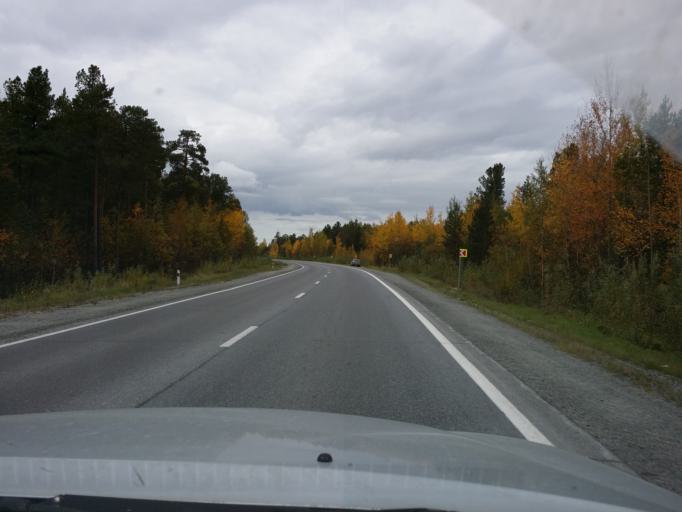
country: RU
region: Khanty-Mansiyskiy Avtonomnyy Okrug
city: Langepas
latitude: 61.2241
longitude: 75.3299
